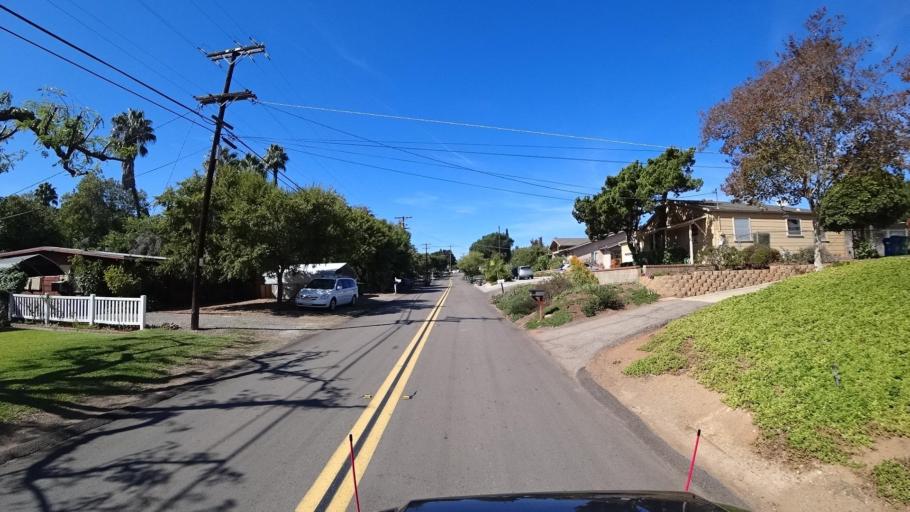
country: US
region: California
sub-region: San Diego County
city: Casa de Oro-Mount Helix
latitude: 32.7506
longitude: -116.9635
